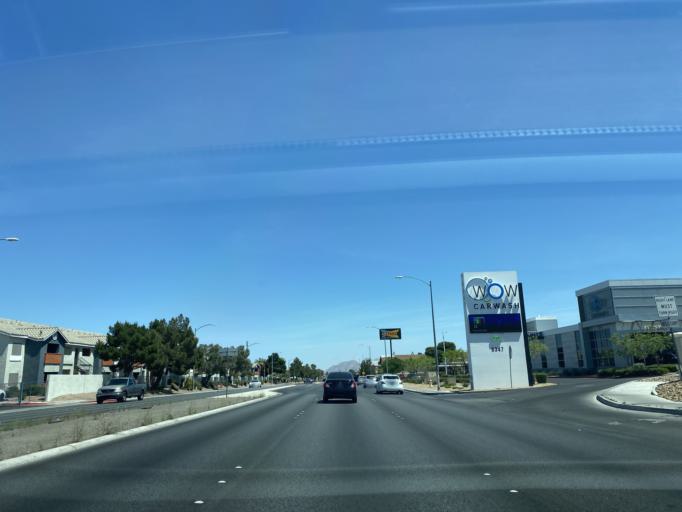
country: US
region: Nevada
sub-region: Clark County
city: Spring Valley
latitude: 36.1958
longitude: -115.2324
